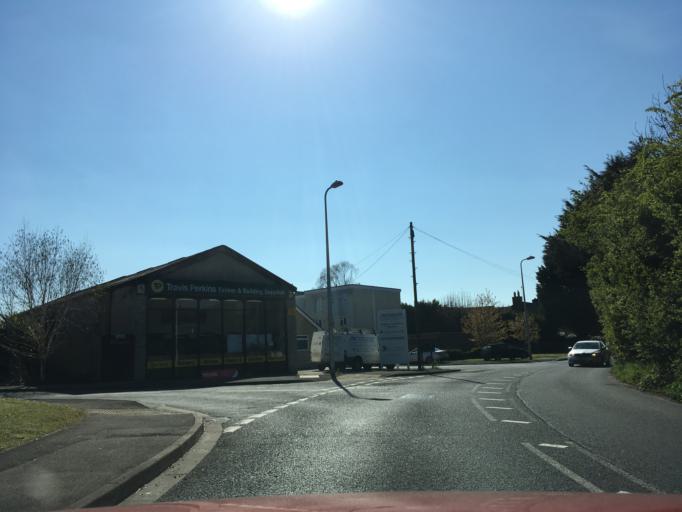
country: GB
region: England
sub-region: North Somerset
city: Portishead
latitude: 51.4764
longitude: -2.7606
